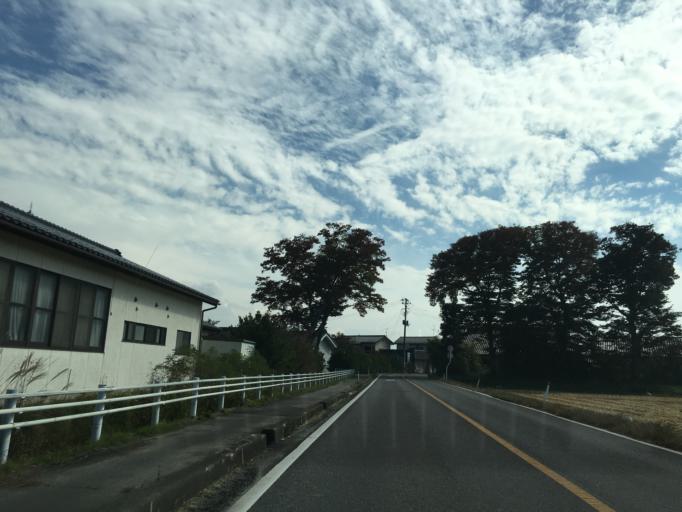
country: JP
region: Fukushima
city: Sukagawa
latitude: 37.2774
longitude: 140.4036
